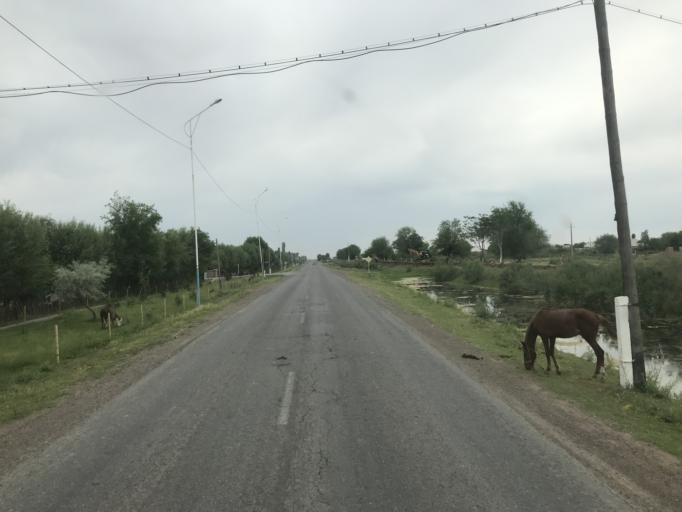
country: KZ
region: Ongtustik Qazaqstan
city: Asykata
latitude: 40.9323
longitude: 68.4081
